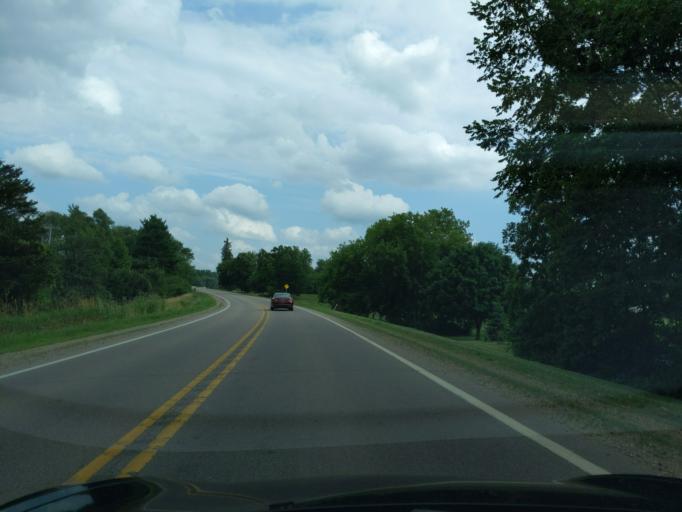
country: US
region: Michigan
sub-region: Eaton County
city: Eaton Rapids
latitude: 42.4613
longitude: -84.6586
